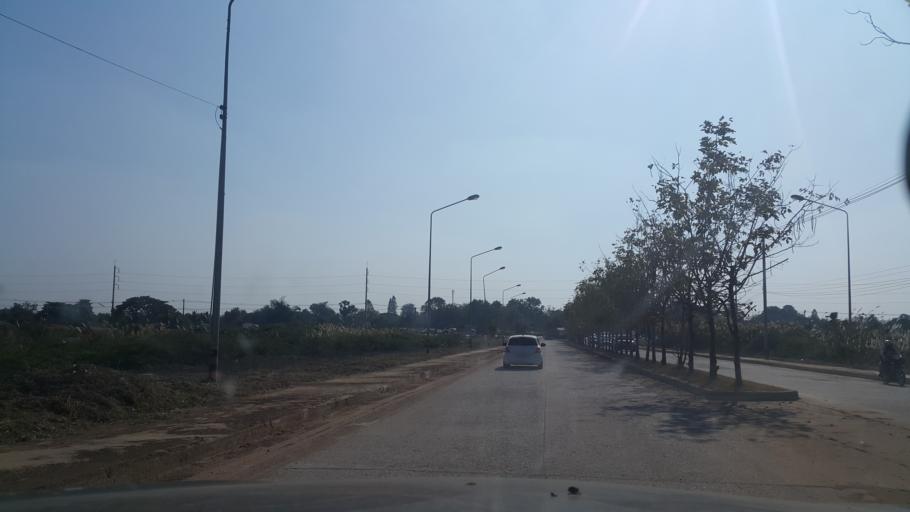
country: TH
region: Khon Kaen
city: Khon Kaen
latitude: 16.5090
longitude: 102.8677
